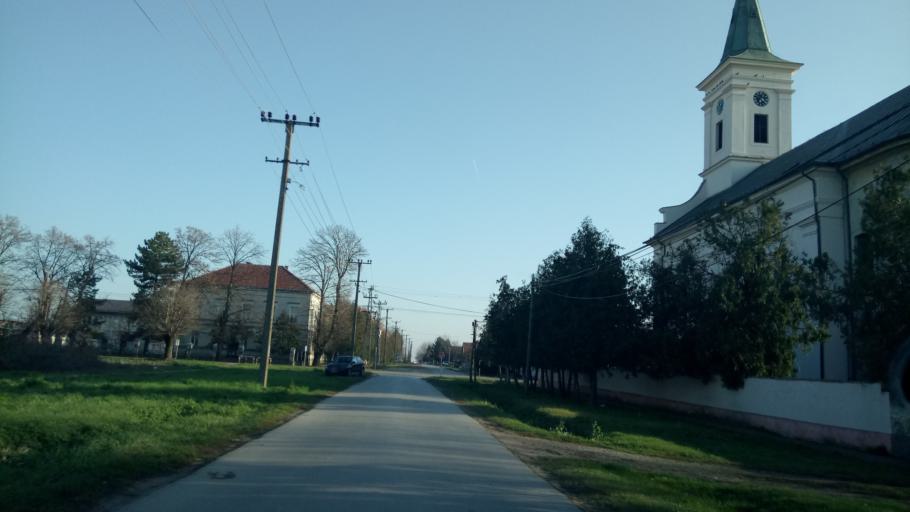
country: RS
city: Novi Slankamen
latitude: 45.1249
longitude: 20.2364
